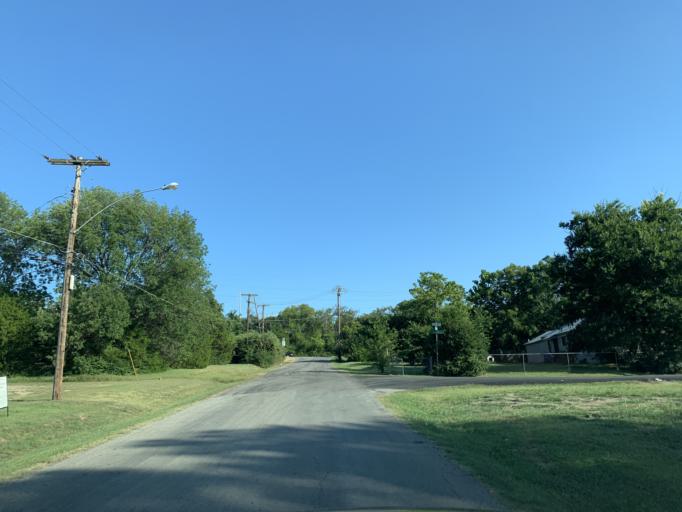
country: US
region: Texas
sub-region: Dallas County
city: Hutchins
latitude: 32.6691
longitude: -96.7730
